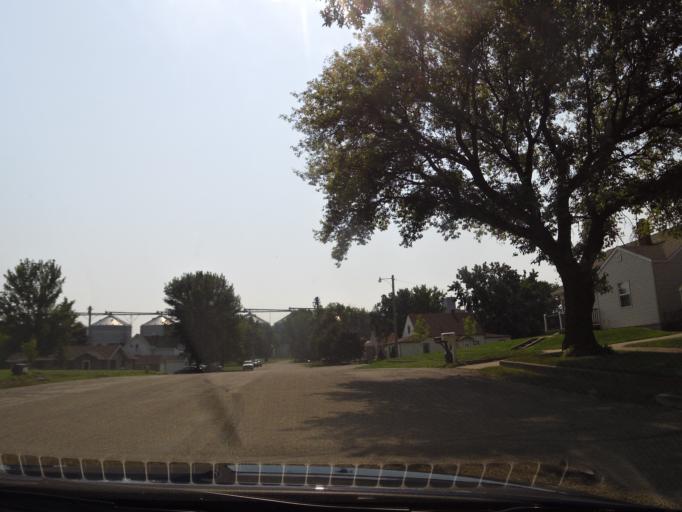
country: US
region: South Dakota
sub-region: Roberts County
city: Sisseton
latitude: 46.0748
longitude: -97.1461
